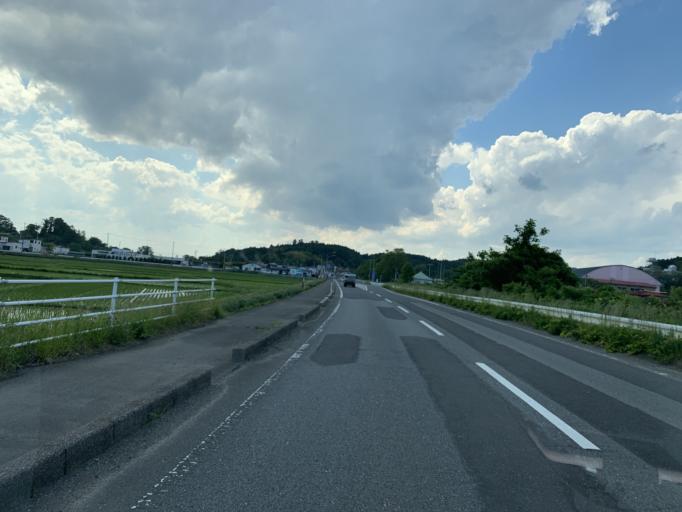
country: JP
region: Miyagi
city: Wakuya
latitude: 38.5428
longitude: 141.1479
